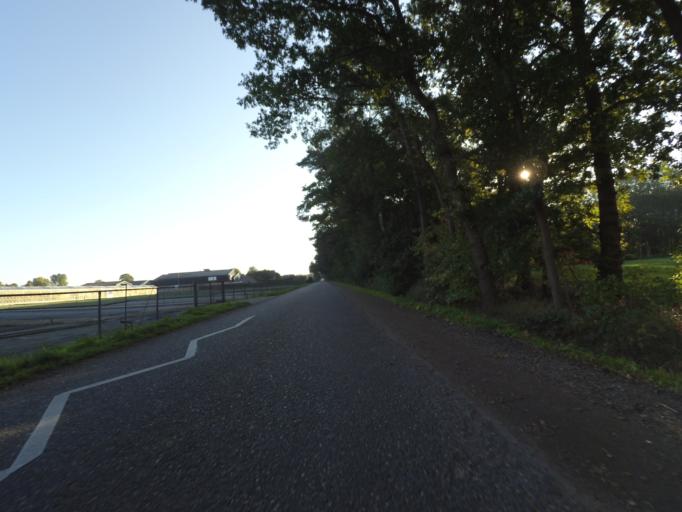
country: NL
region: Gelderland
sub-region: Gemeente Barneveld
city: Zwartebroek
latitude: 52.1995
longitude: 5.5259
